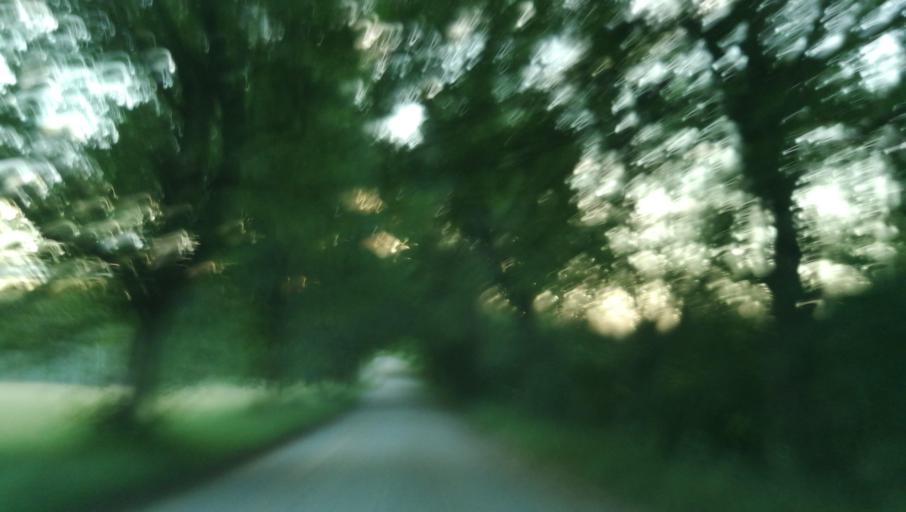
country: LV
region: Amatas Novads
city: Drabesi
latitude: 57.2568
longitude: 25.1650
